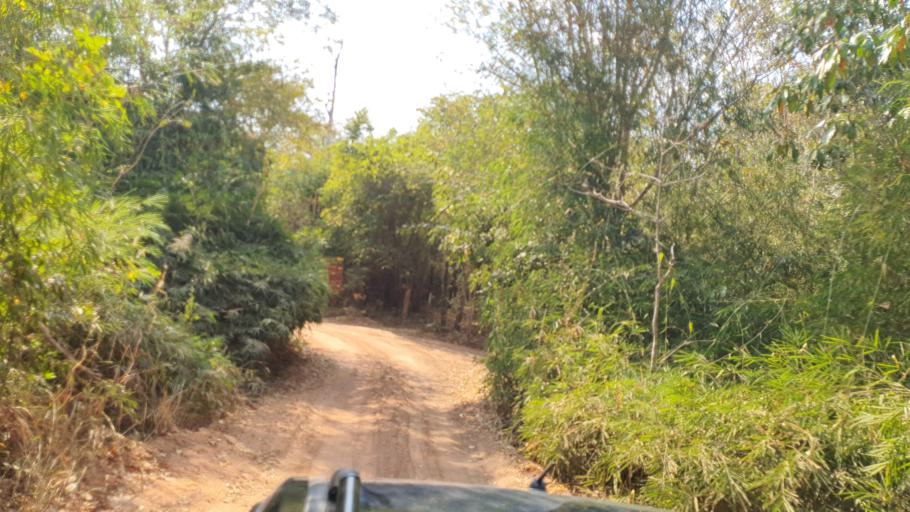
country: TH
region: Changwat Bueng Kan
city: Si Wilai
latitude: 18.2683
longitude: 103.7990
